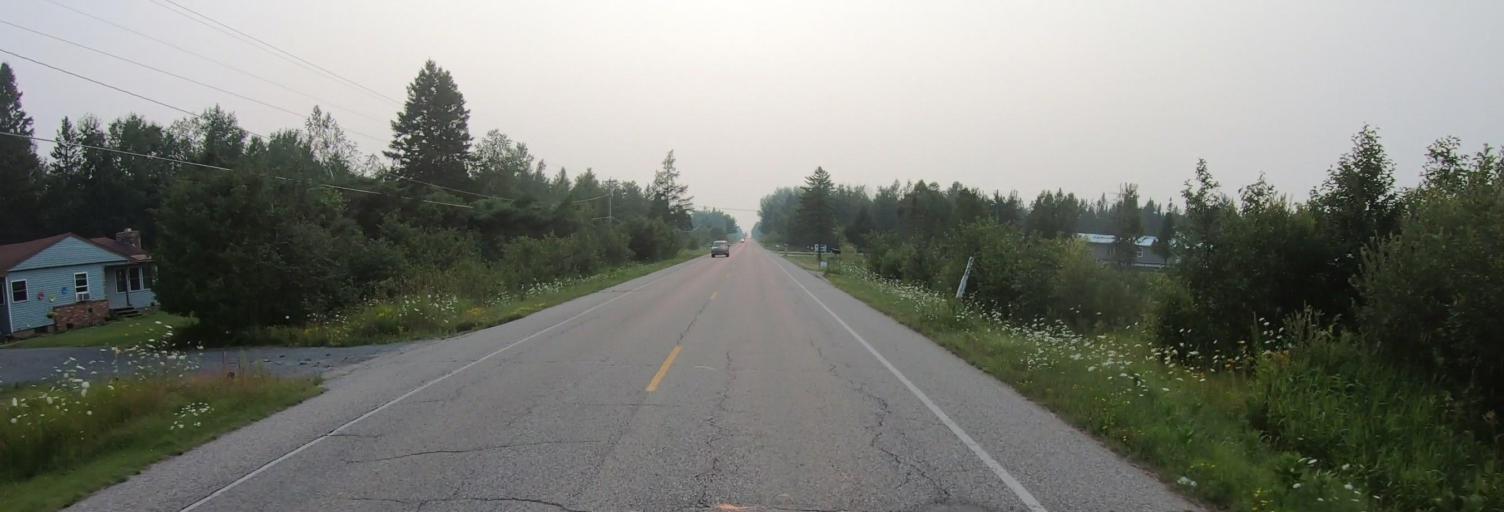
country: US
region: Michigan
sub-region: Chippewa County
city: Sault Ste. Marie
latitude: 46.4188
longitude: -84.4933
